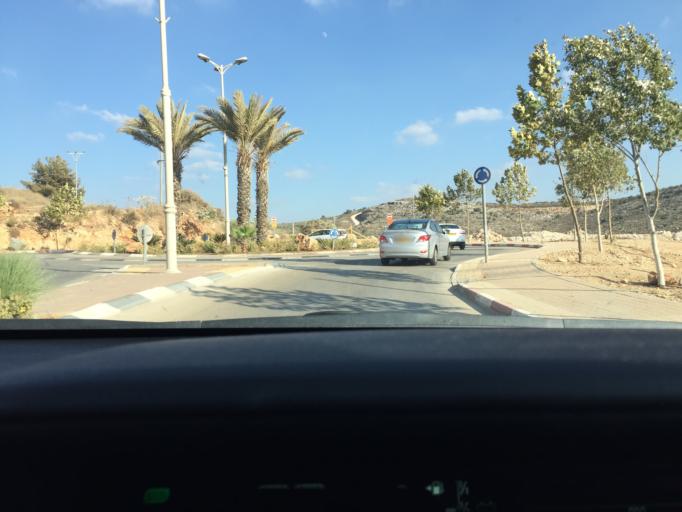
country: PS
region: West Bank
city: Al Lubban al Gharbi
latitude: 32.0305
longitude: 35.0505
